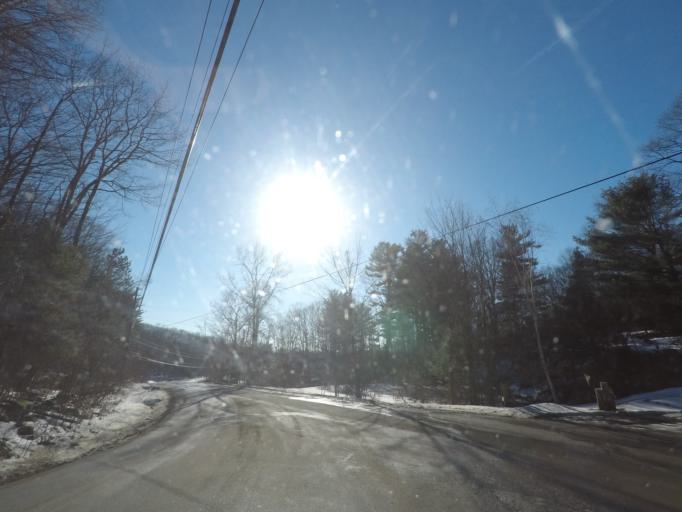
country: US
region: New York
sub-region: Rensselaer County
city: Averill Park
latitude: 42.6366
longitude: -73.5253
